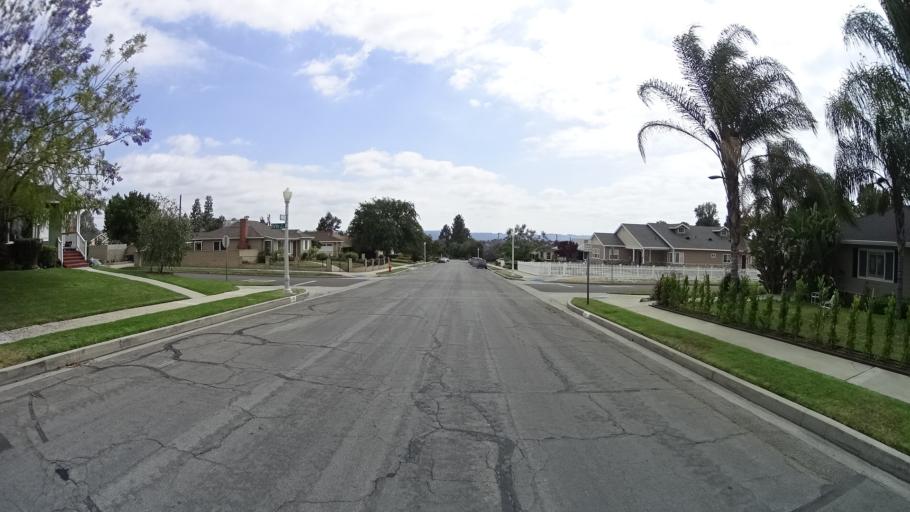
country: US
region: California
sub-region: Los Angeles County
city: Burbank
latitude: 34.1943
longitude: -118.3181
